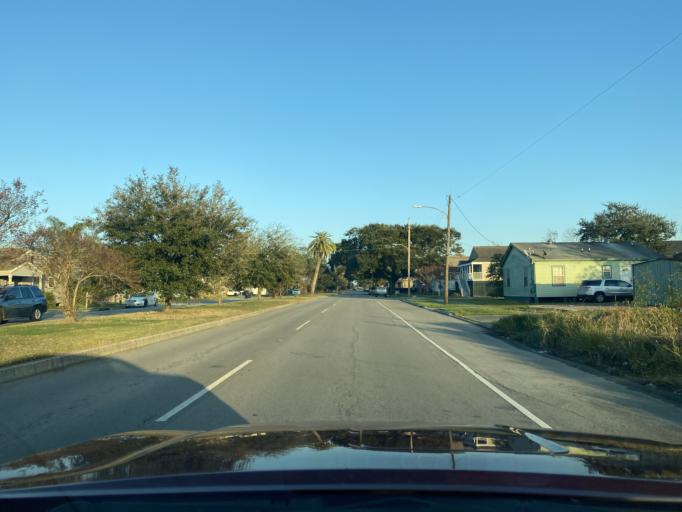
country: US
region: Louisiana
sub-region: Orleans Parish
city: New Orleans
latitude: 30.0223
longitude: -90.0560
